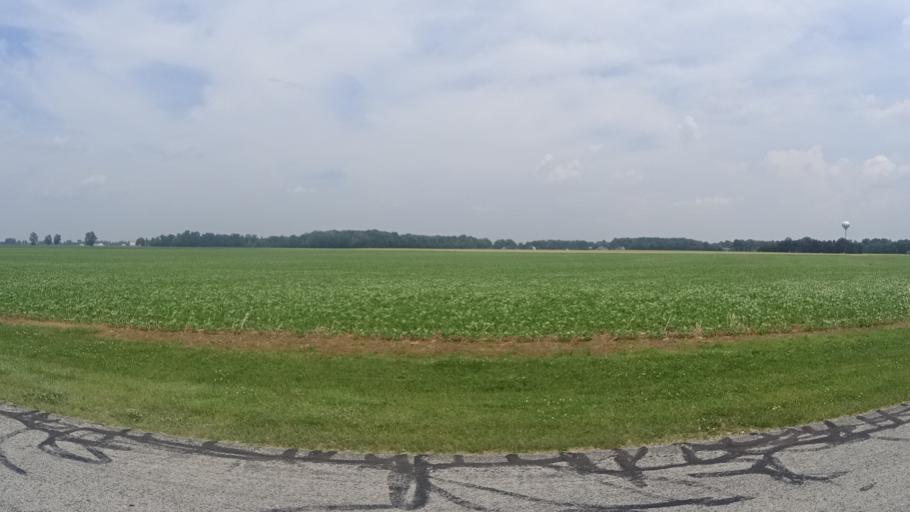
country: US
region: Ohio
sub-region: Erie County
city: Milan
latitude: 41.3000
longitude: -82.6527
